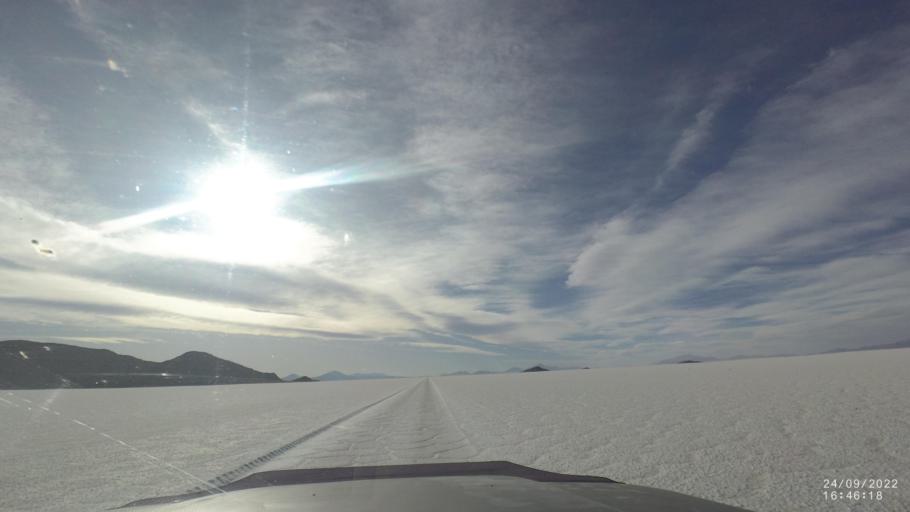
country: BO
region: Potosi
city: Colchani
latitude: -20.1392
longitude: -67.7881
